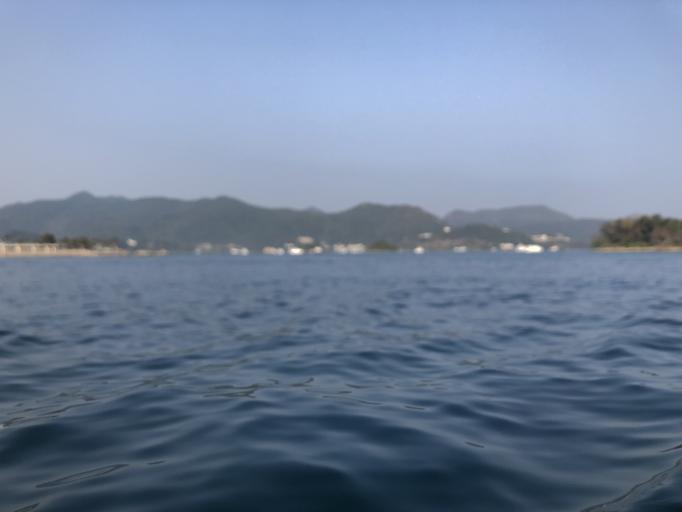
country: HK
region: Sai Kung
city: Sai Kung
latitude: 22.3804
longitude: 114.2760
